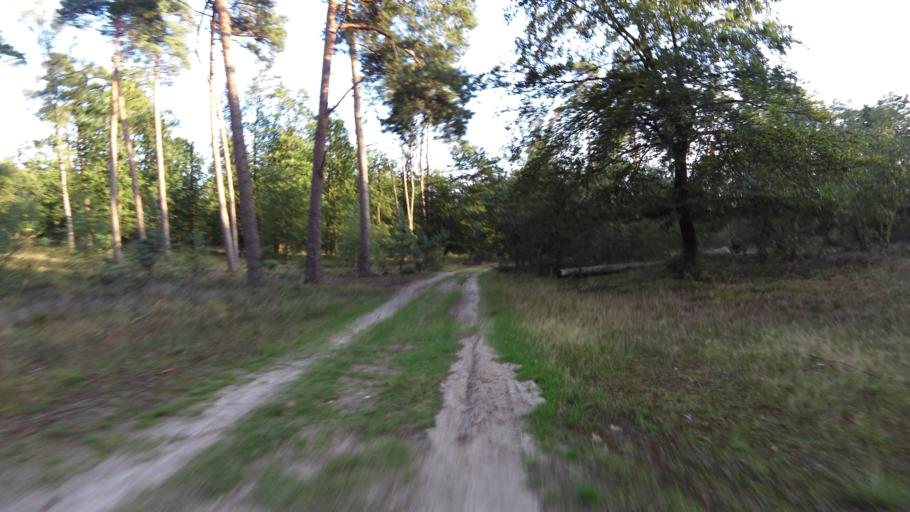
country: NL
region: Gelderland
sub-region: Gemeente Epe
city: Vaassen
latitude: 52.2959
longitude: 5.8774
